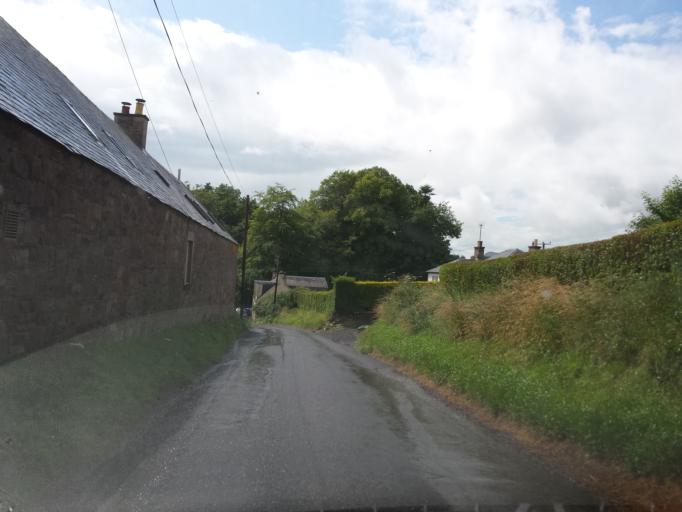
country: GB
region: Scotland
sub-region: The Scottish Borders
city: Saint Boswells
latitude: 55.5940
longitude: -2.6439
